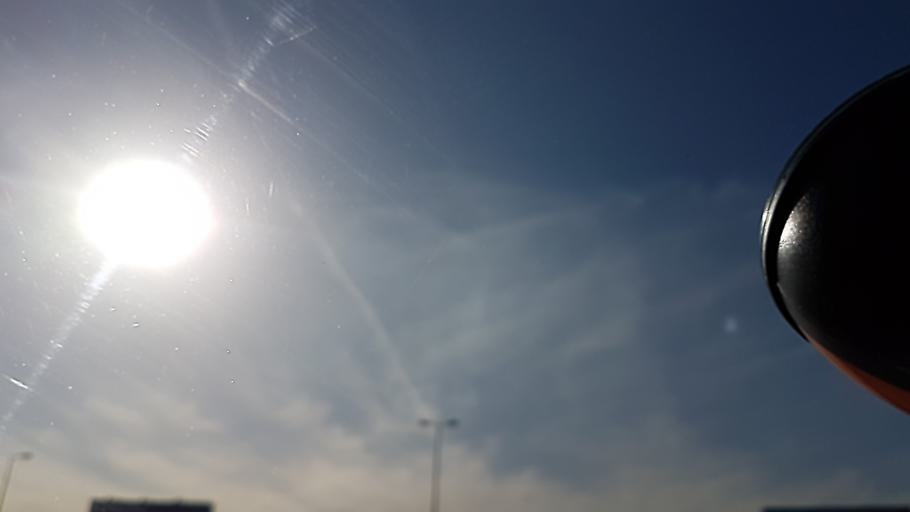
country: LB
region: Beyrouth
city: Beirut
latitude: 33.8641
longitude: 35.4941
